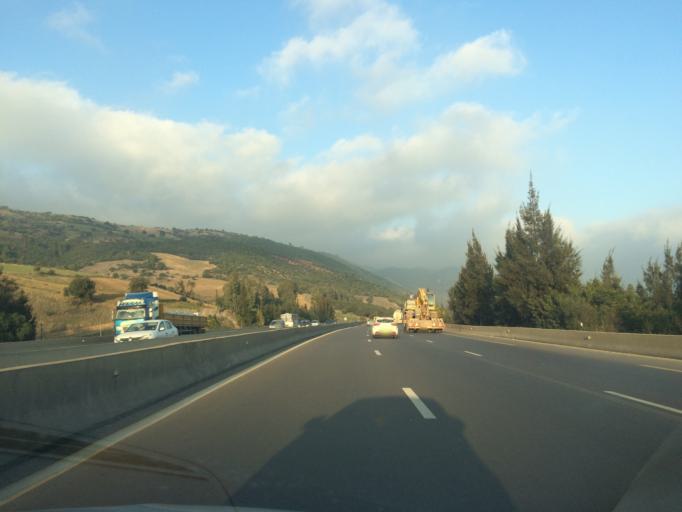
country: DZ
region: Tipaza
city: Hadjout
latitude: 36.3804
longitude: 2.4802
